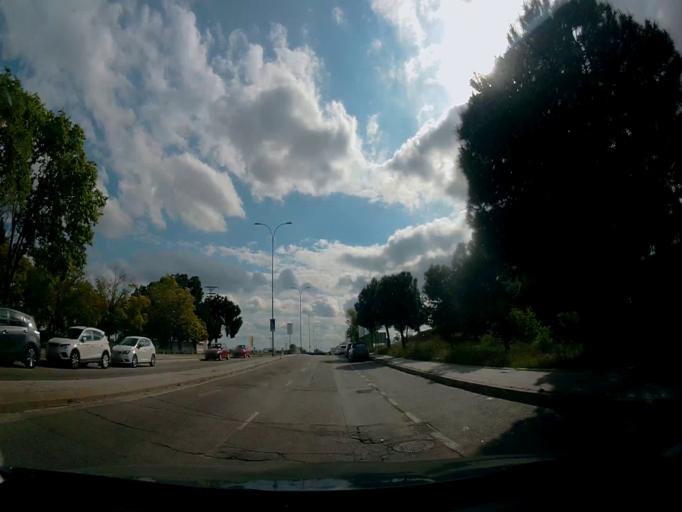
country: ES
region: Madrid
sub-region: Provincia de Madrid
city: Alcorcon
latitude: 40.3409
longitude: -3.8431
